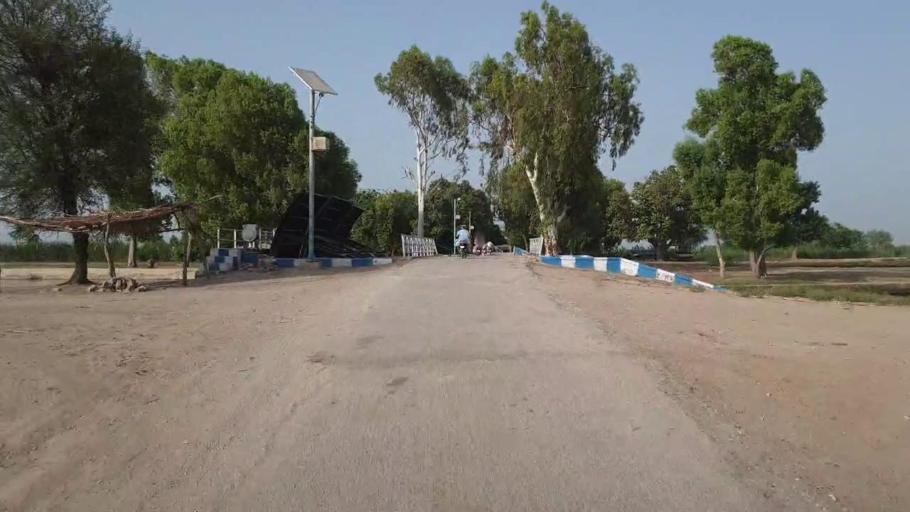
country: PK
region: Sindh
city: Daur
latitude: 26.3494
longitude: 68.1726
